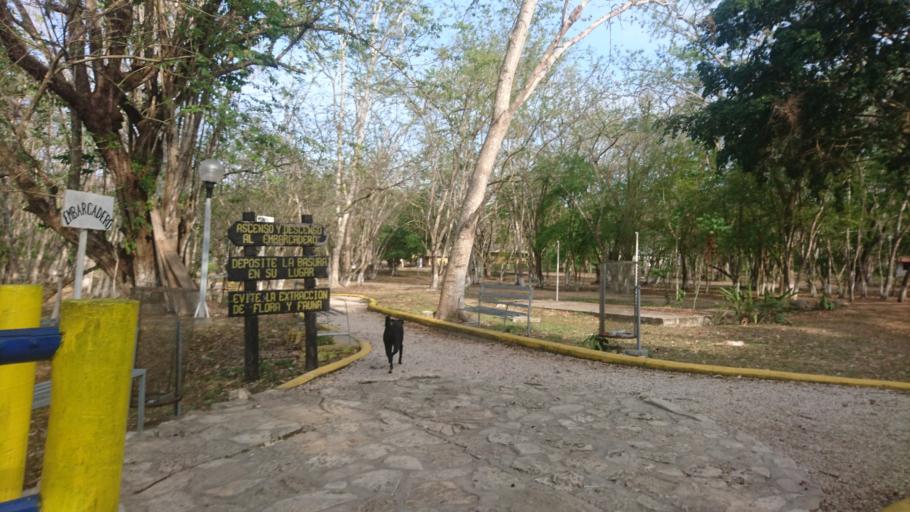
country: MX
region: Chiapas
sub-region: Ocosingo
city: Frontera Corozal
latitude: 16.8234
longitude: -90.8867
